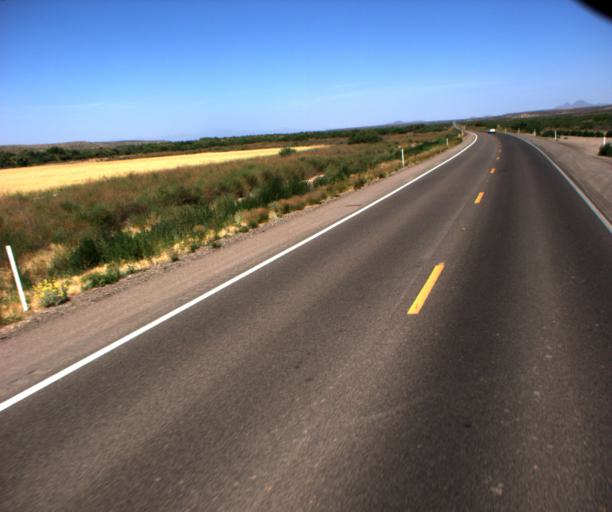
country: US
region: Arizona
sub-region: Graham County
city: Bylas
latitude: 33.1747
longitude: -110.1414
